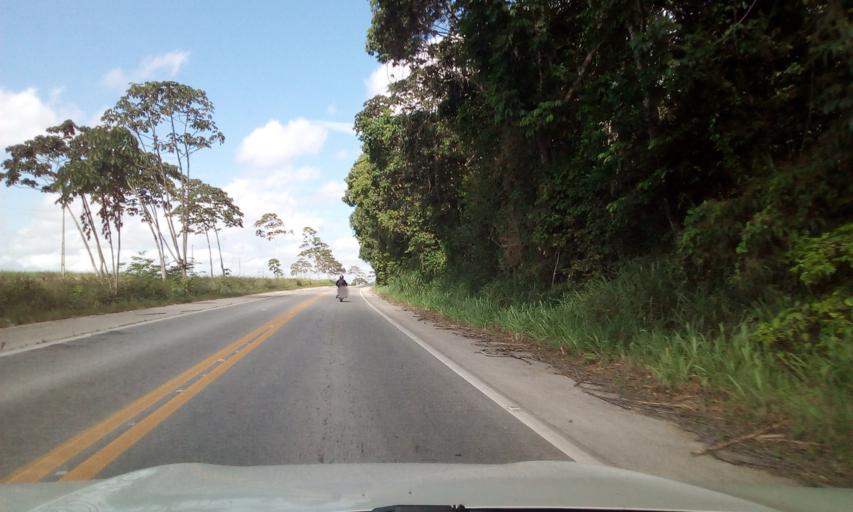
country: BR
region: Alagoas
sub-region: Pilar
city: Pilar
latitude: -9.5139
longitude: -35.9329
